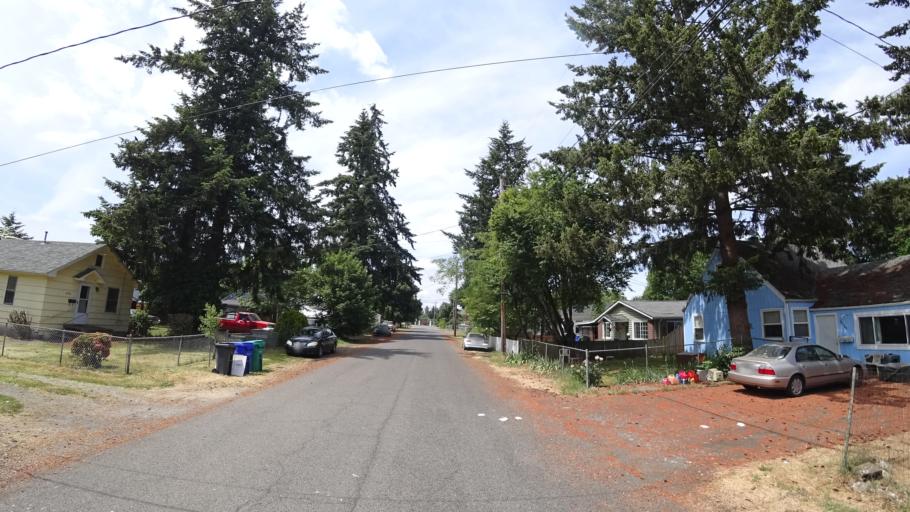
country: US
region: Oregon
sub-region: Multnomah County
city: Lents
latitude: 45.4654
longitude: -122.5921
